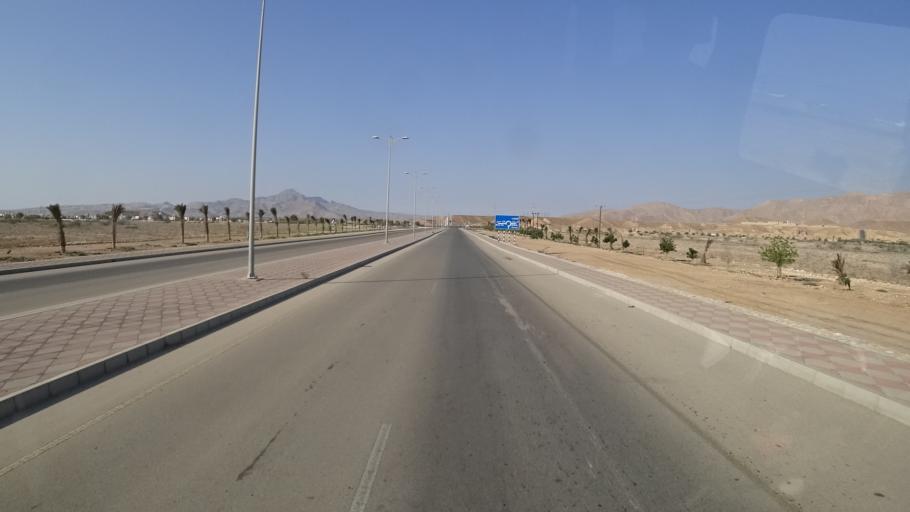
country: OM
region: Ash Sharqiyah
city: Sur
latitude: 22.5789
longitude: 59.4683
